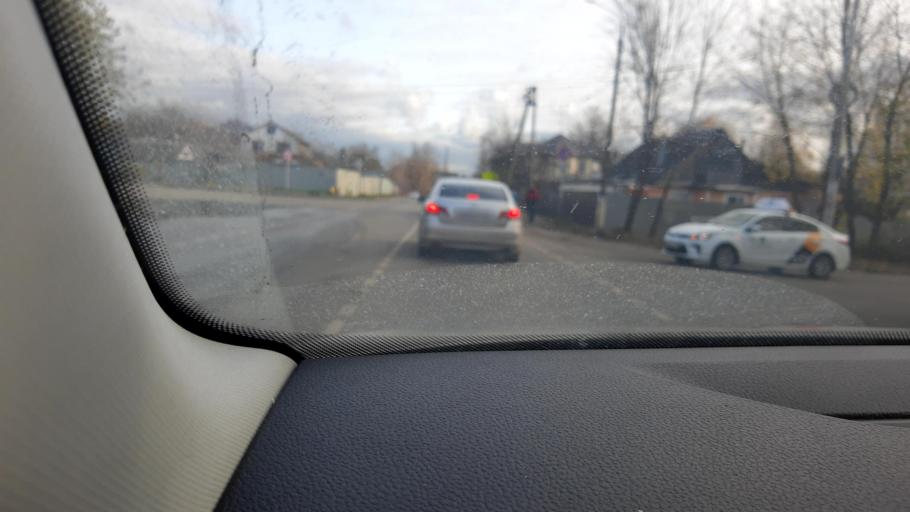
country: RU
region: Moskovskaya
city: Shcherbinka
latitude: 55.4728
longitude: 37.5753
